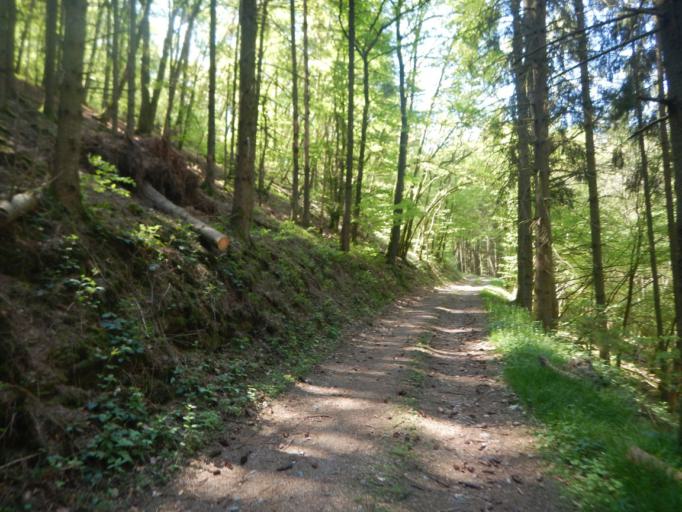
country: LU
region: Diekirch
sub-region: Canton de Diekirch
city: Bourscheid
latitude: 49.8905
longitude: 6.0888
